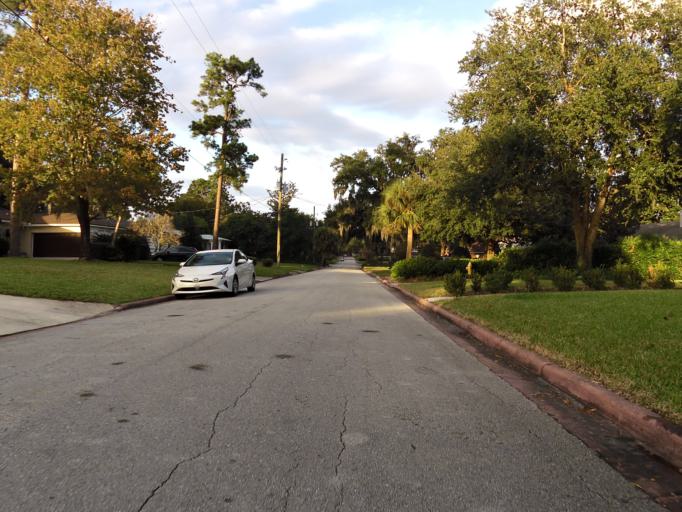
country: US
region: Florida
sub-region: Duval County
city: Jacksonville
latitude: 30.2823
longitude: -81.6599
